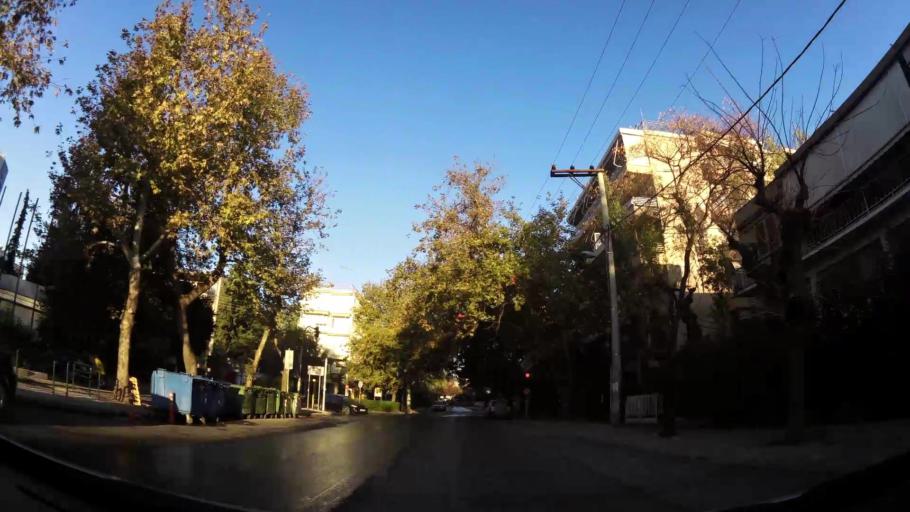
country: GR
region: Attica
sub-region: Nomarchia Athinas
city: Marousi
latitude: 38.0480
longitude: 23.8037
